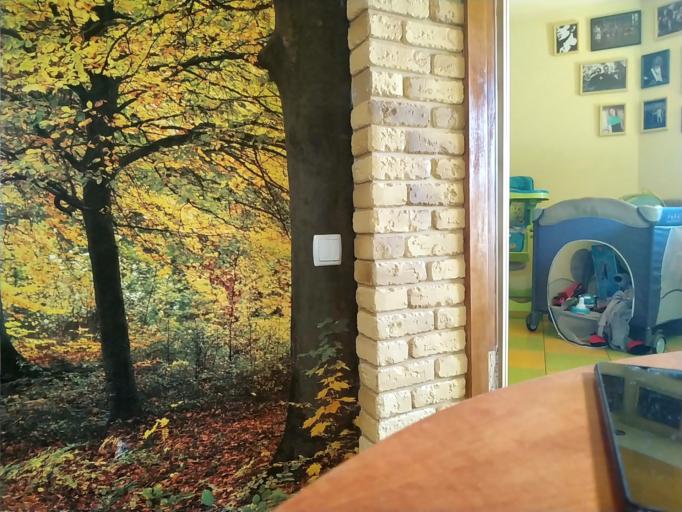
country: RU
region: Tverskaya
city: Kuzhenkino
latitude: 57.5270
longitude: 34.1164
